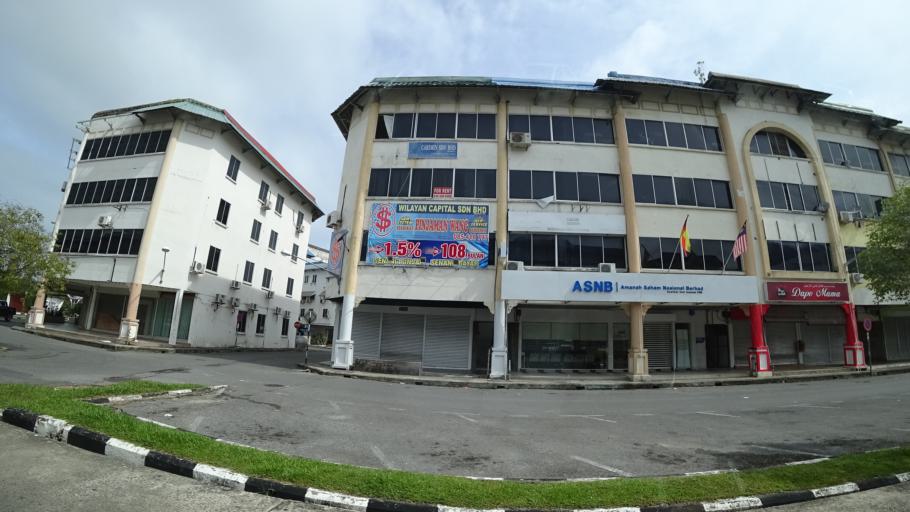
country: MY
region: Sarawak
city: Miri
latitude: 4.3988
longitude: 113.9867
